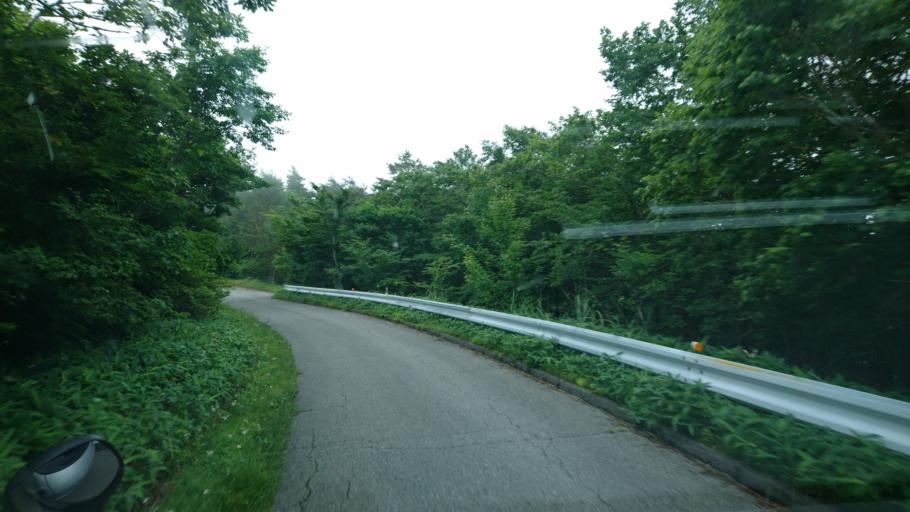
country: JP
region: Iwate
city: Ofunato
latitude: 39.1444
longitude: 141.7539
